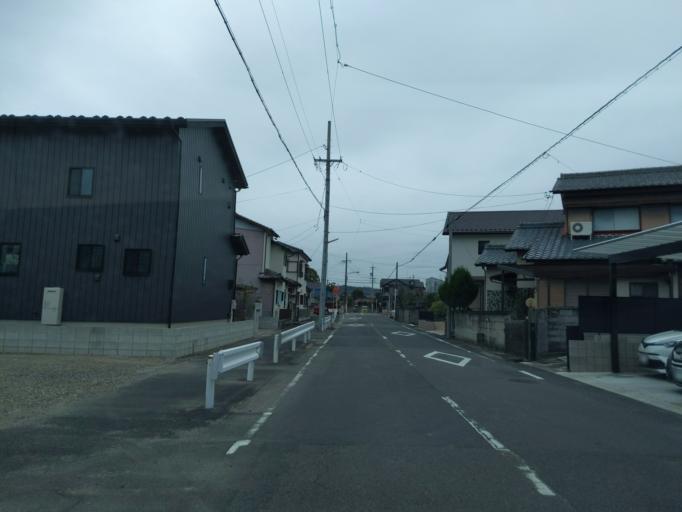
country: JP
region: Aichi
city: Kasugai
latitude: 35.2505
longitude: 136.9895
